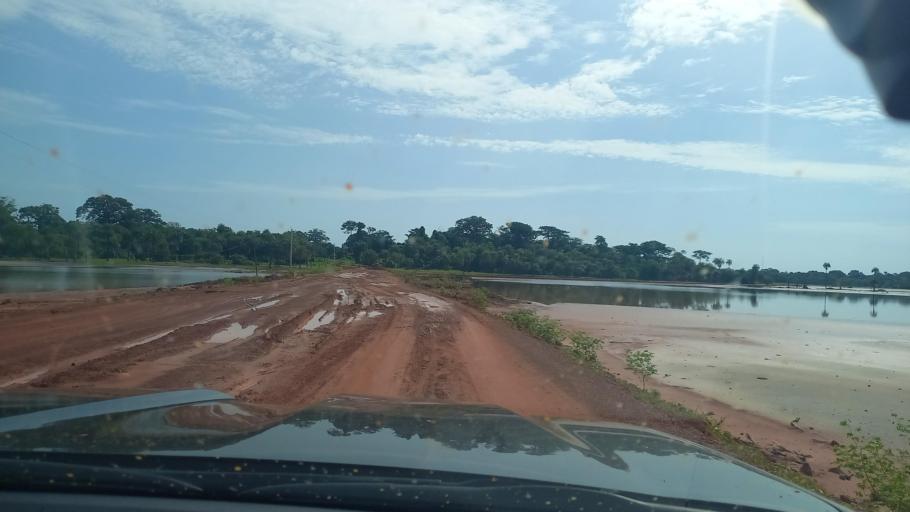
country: SN
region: Ziguinchor
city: Ziguinchor
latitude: 12.6735
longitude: -16.2033
